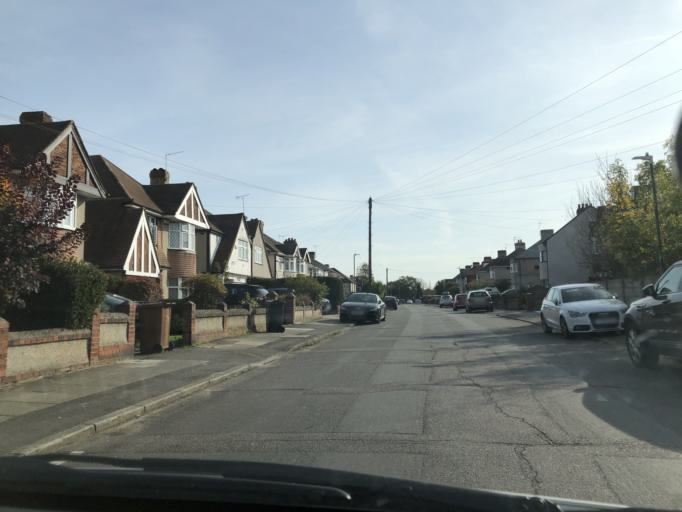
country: GB
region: England
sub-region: Kent
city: Dartford
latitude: 51.4418
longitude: 0.1878
